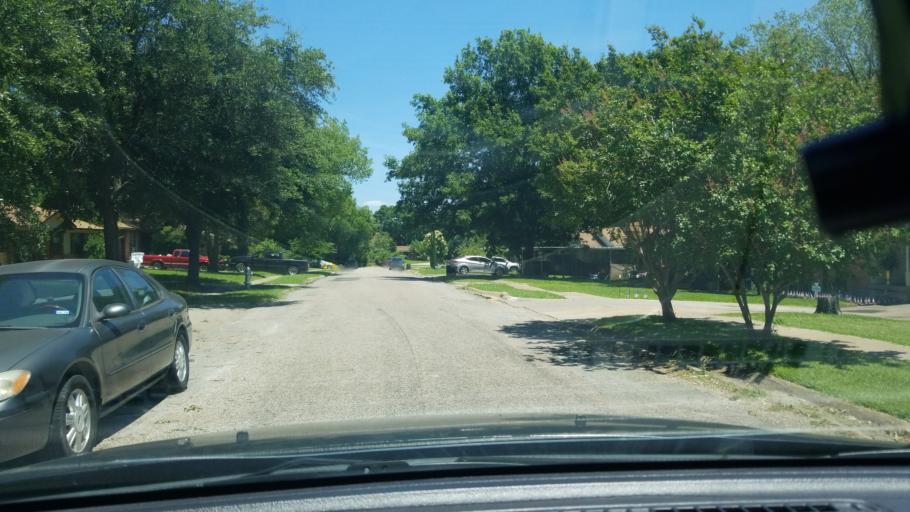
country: US
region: Texas
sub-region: Dallas County
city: Mesquite
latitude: 32.7717
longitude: -96.6043
